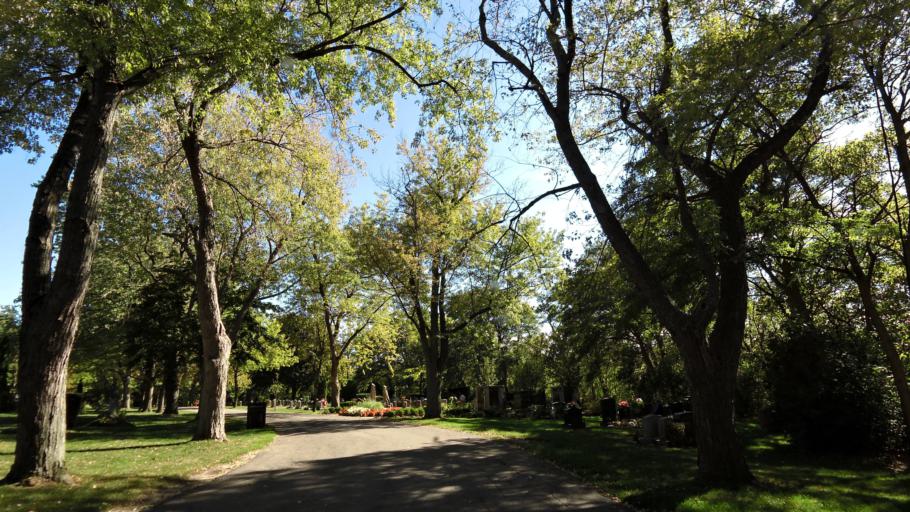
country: CA
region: Ontario
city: Mississauga
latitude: 43.5811
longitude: -79.7055
